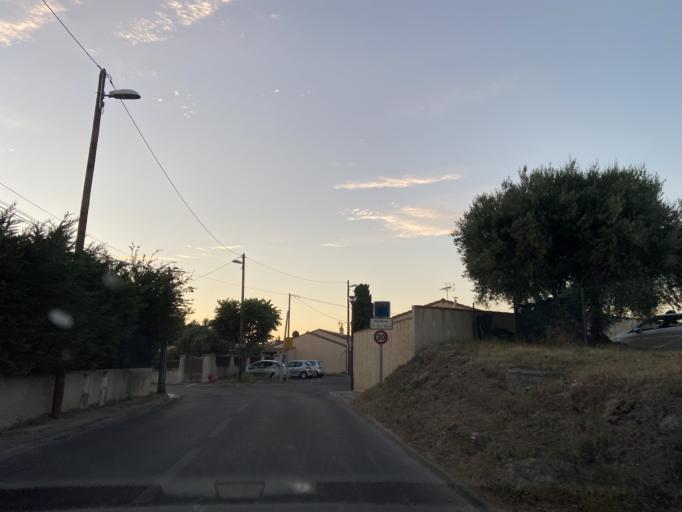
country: FR
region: Provence-Alpes-Cote d'Azur
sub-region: Departement des Bouches-du-Rhone
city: Plan-de-Cuques
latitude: 43.3265
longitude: 5.4489
